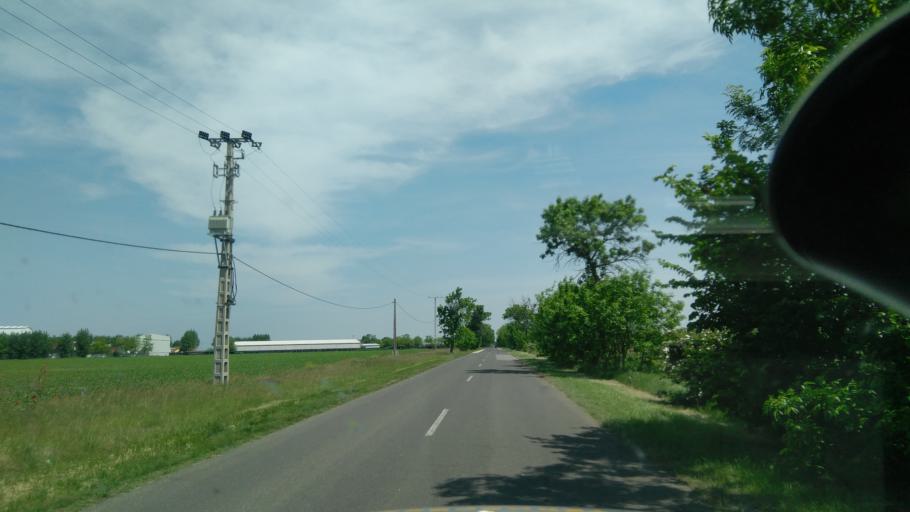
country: HU
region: Csongrad
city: Szekkutas
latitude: 46.5707
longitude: 20.5588
